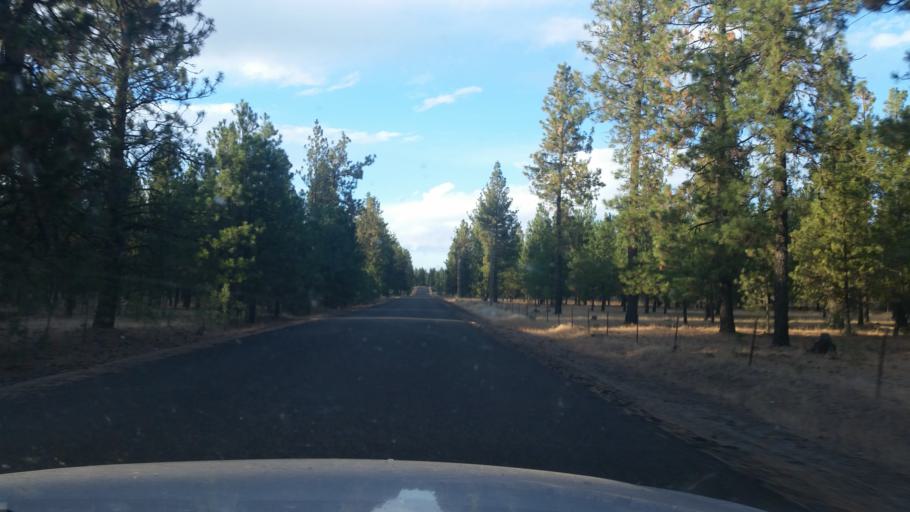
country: US
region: Washington
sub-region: Spokane County
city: Medical Lake
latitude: 47.4430
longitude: -117.7897
